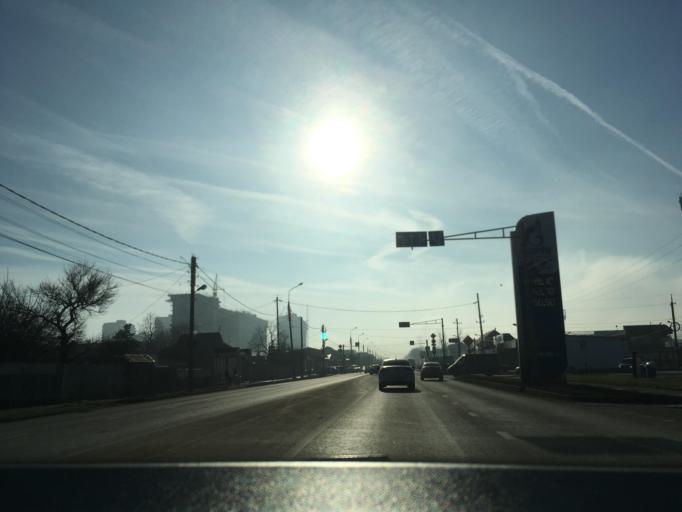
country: RU
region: Krasnodarskiy
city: Krasnodar
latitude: 45.1117
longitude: 39.0121
